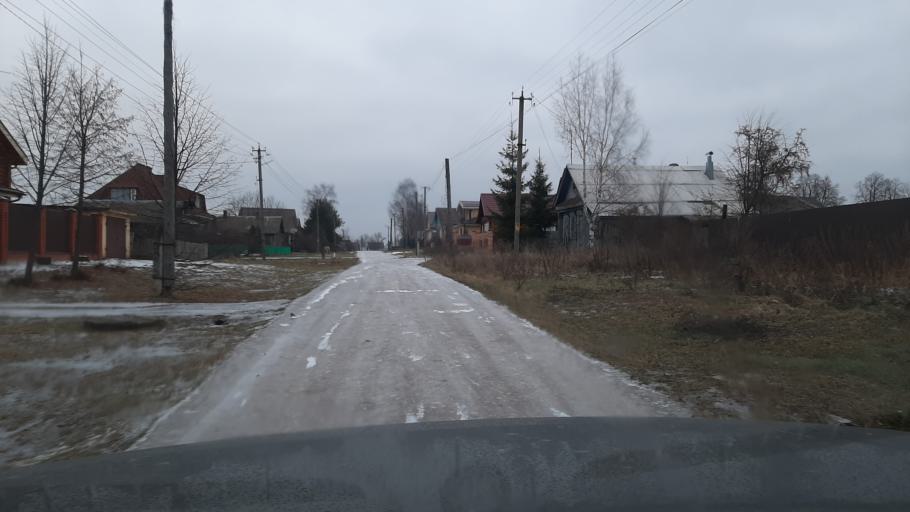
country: RU
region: Ivanovo
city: Shuya
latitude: 56.9934
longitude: 41.4068
